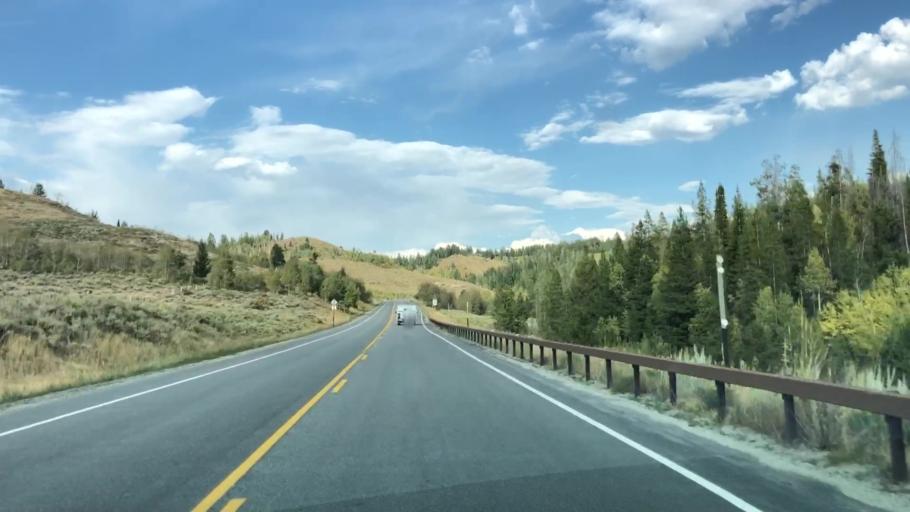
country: US
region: Wyoming
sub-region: Sublette County
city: Pinedale
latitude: 43.1363
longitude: -110.2254
